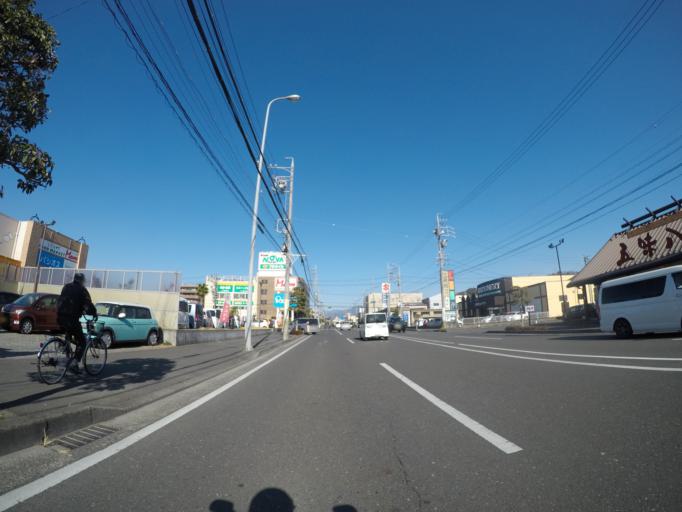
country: JP
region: Shizuoka
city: Shizuoka-shi
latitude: 34.9831
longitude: 138.3661
